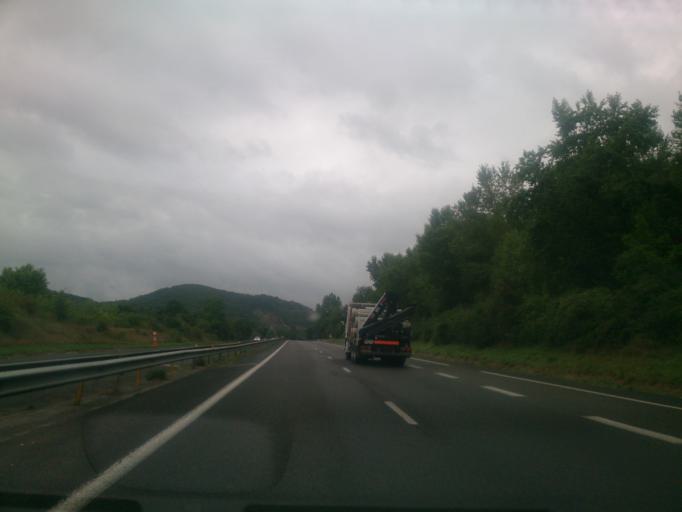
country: FR
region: Midi-Pyrenees
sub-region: Departement de la Haute-Garonne
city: Martres-Tolosane
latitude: 43.1843
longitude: 0.9798
